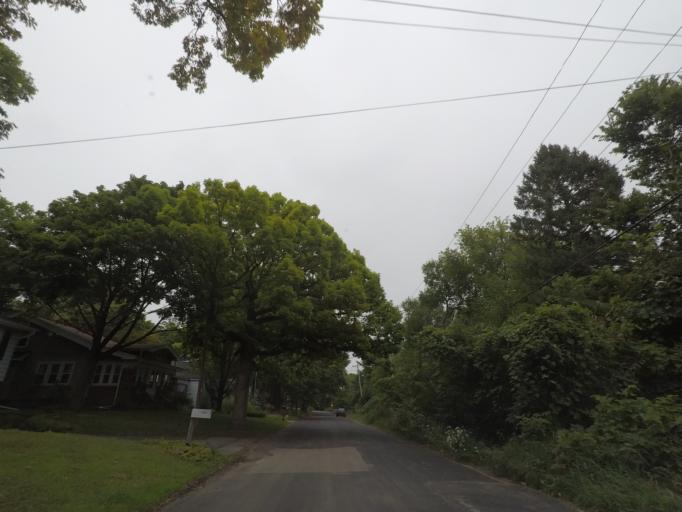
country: US
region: Wisconsin
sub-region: Dane County
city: Maple Bluff
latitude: 43.1117
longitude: -89.3342
